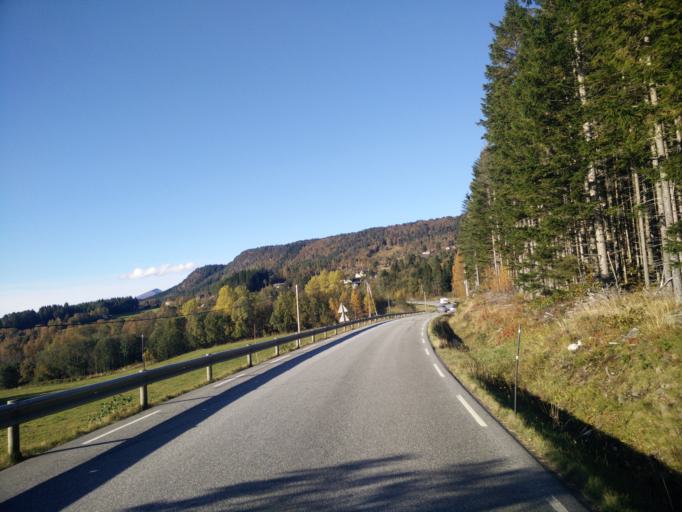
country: NO
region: More og Romsdal
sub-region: Halsa
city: Liaboen
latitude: 63.1138
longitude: 8.3224
